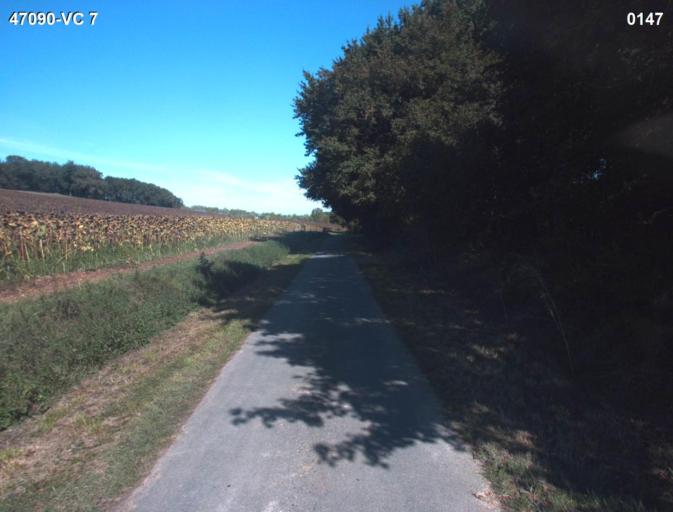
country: FR
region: Aquitaine
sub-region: Departement du Lot-et-Garonne
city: Nerac
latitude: 44.1682
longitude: 0.3628
